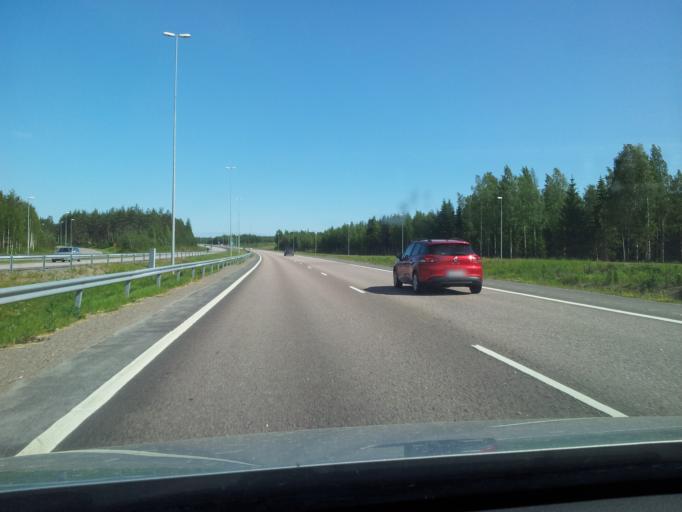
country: FI
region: Uusimaa
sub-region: Loviisa
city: Lovisa
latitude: 60.4626
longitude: 26.1457
